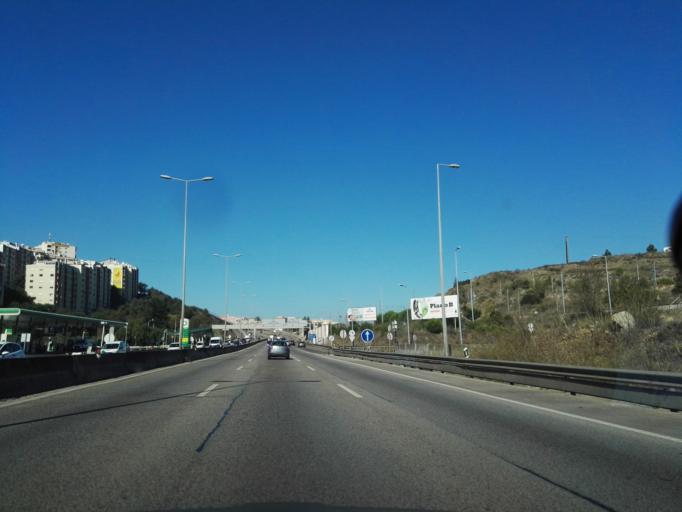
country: PT
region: Lisbon
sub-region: Sintra
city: Cacem
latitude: 38.7612
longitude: -9.2955
